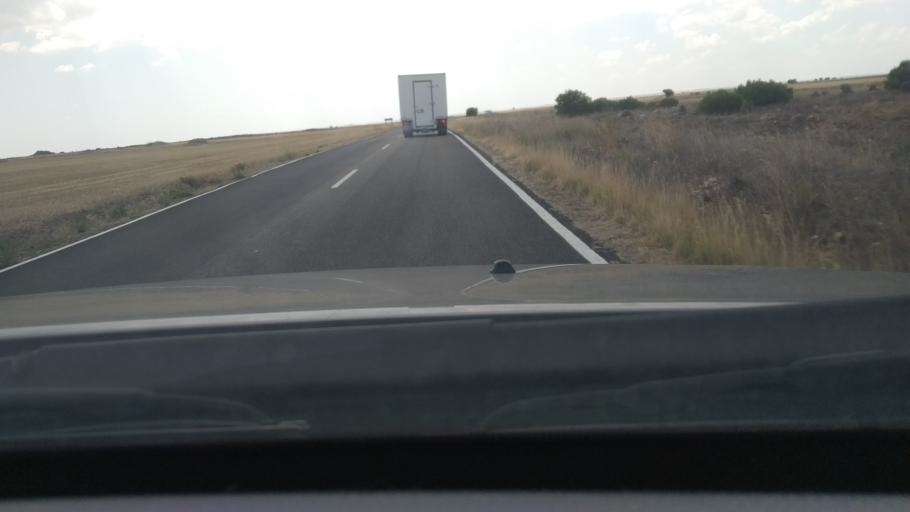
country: ES
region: Castille and Leon
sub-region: Provincia de Burgos
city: Iglesiarrubia
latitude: 41.9476
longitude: -3.8400
